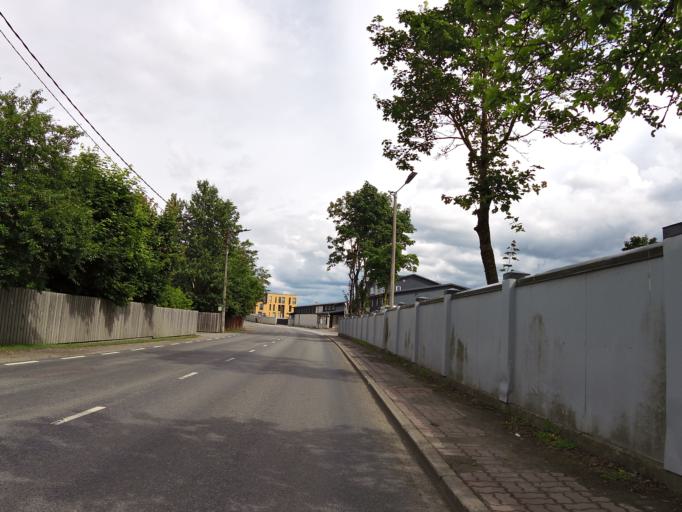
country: EE
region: Harju
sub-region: Saue vald
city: Laagri
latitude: 59.3832
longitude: 24.6601
